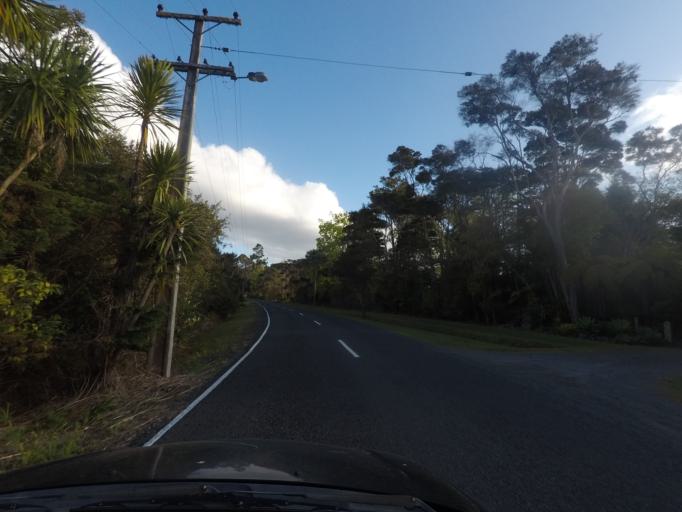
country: NZ
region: Auckland
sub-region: Auckland
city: Waitakere
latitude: -36.9205
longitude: 174.6153
